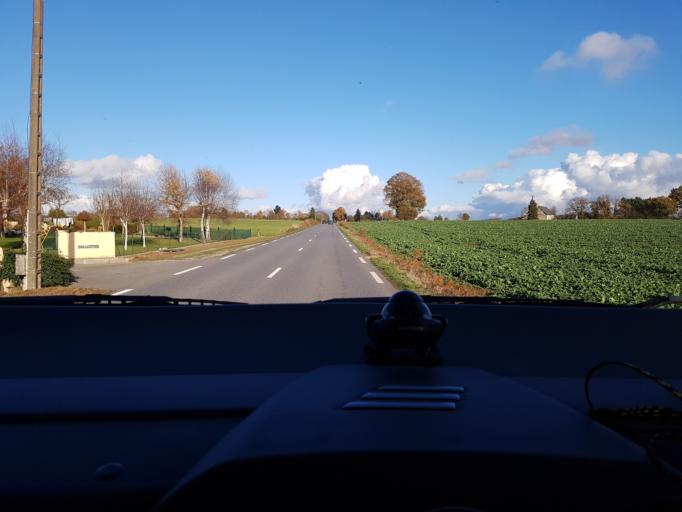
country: FR
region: Brittany
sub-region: Departement d'Ille-et-Vilaine
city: Pire-sur-Seiche
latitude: 48.0166
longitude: -1.4129
